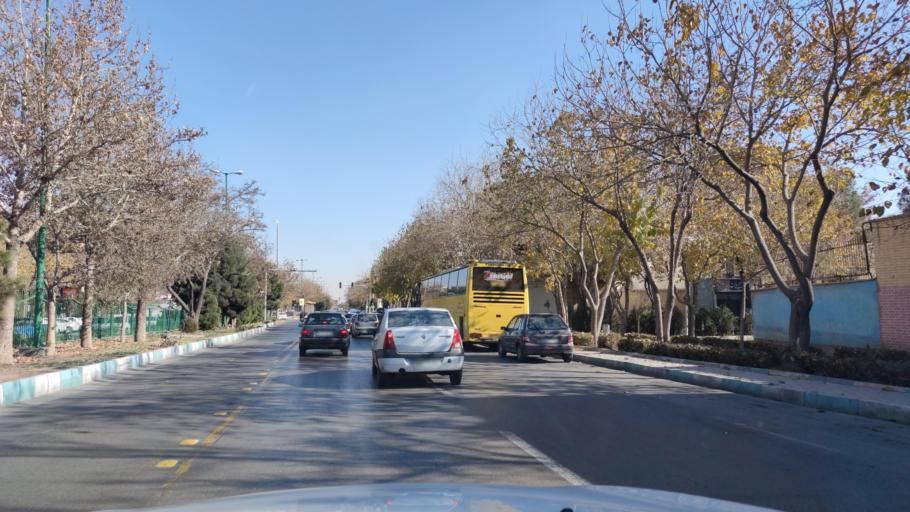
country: IR
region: Isfahan
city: Isfahan
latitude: 32.6788
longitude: 51.6770
